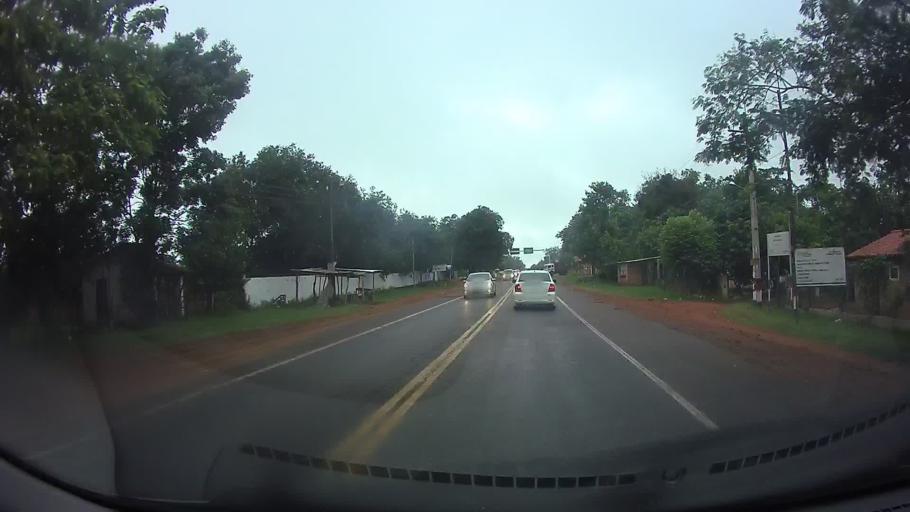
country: PY
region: Central
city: Ita
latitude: -25.5261
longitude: -57.3406
